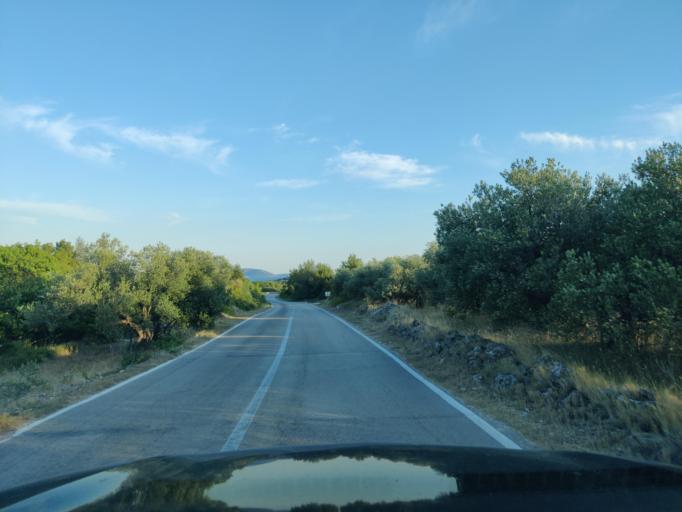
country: HR
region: Sibensko-Kniniska
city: Tribunj
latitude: 43.7757
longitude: 15.7271
